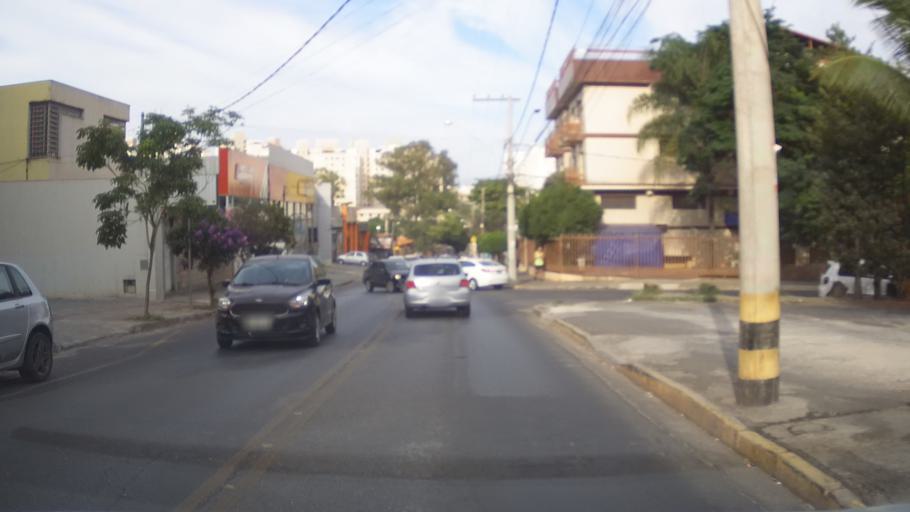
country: BR
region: Minas Gerais
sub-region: Belo Horizonte
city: Belo Horizonte
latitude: -19.8747
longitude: -43.9902
